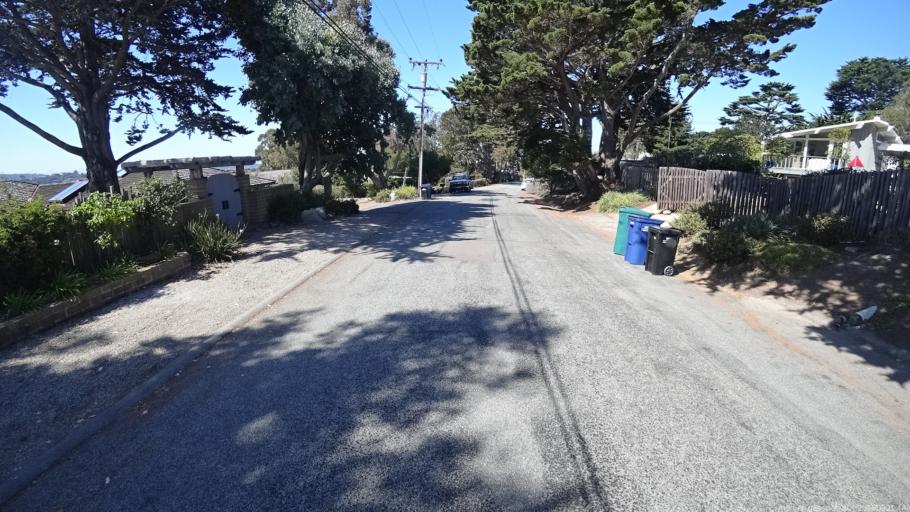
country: US
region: California
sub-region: Monterey County
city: Carmel-by-the-Sea
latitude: 36.5418
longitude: -121.9124
